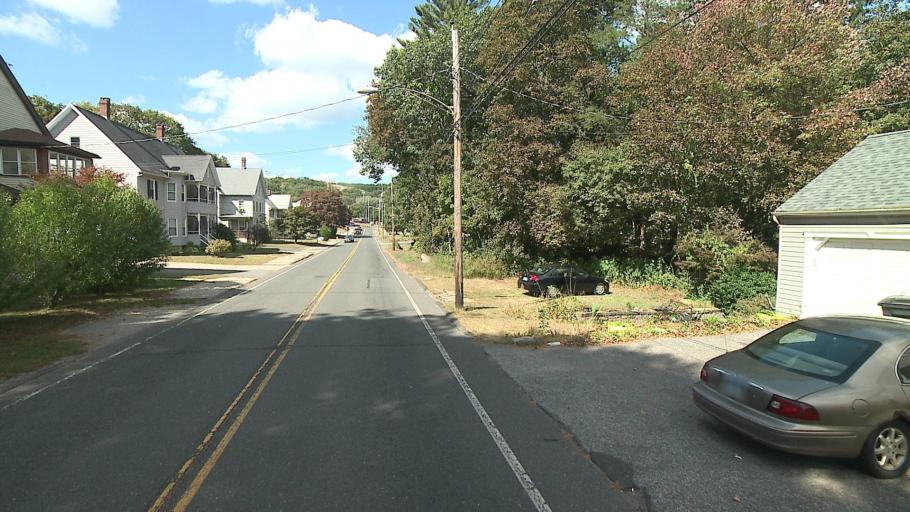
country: US
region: Connecticut
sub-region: New Haven County
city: Ansonia
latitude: 41.3510
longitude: -73.0891
